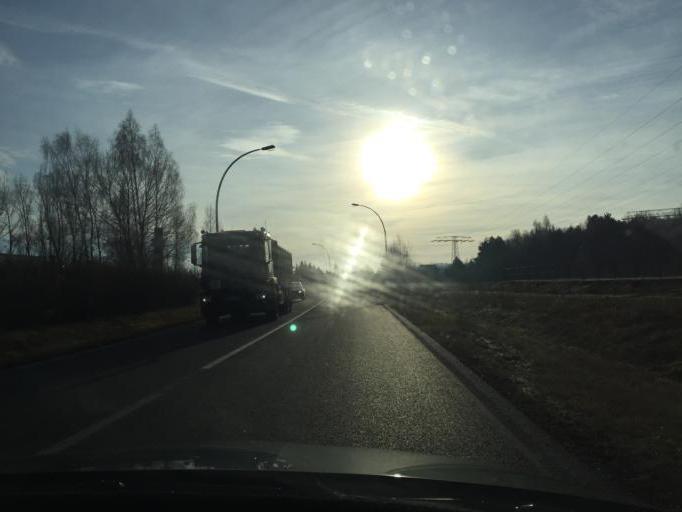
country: DE
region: Brandenburg
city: Eisenhuettenstadt
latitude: 52.1612
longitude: 14.6044
